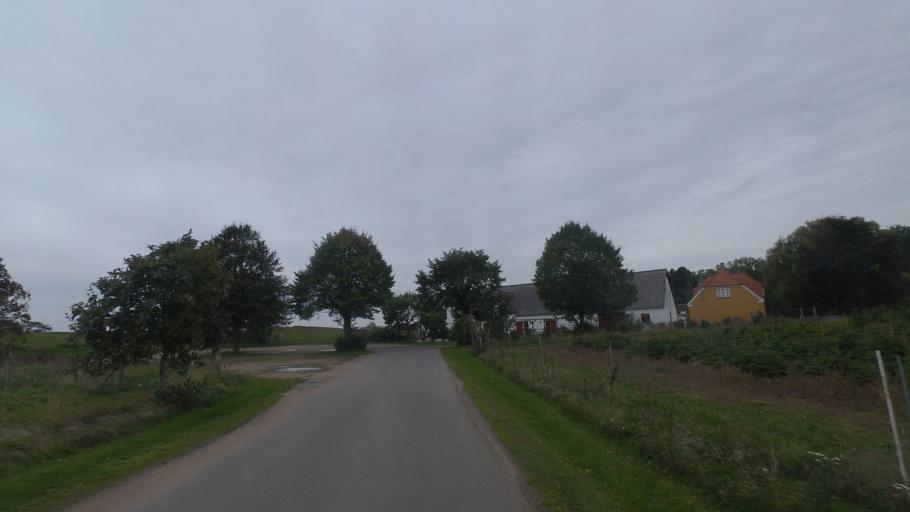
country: DK
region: Capital Region
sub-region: Bornholm Kommune
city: Akirkeby
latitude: 55.0016
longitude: 14.9996
